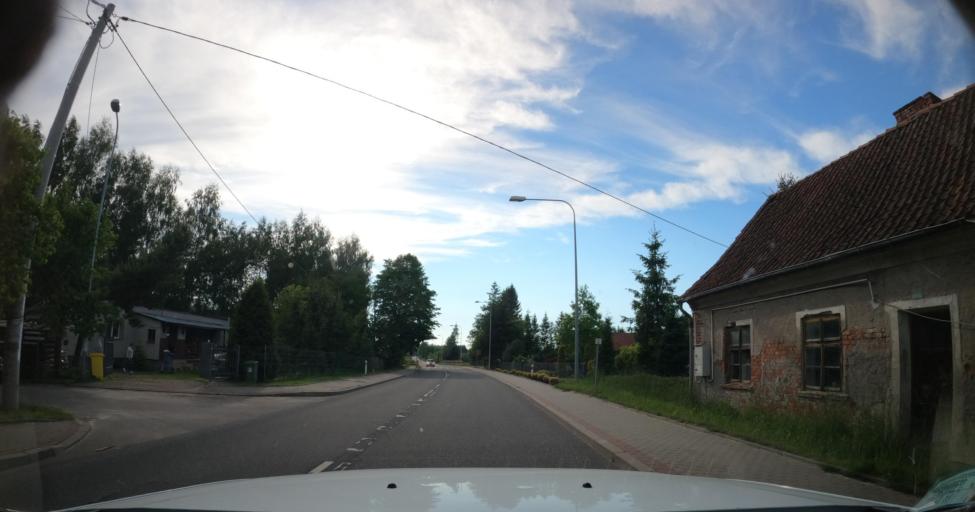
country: PL
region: Warmian-Masurian Voivodeship
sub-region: Powiat ostrodzki
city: Morag
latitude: 54.0811
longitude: 19.8989
